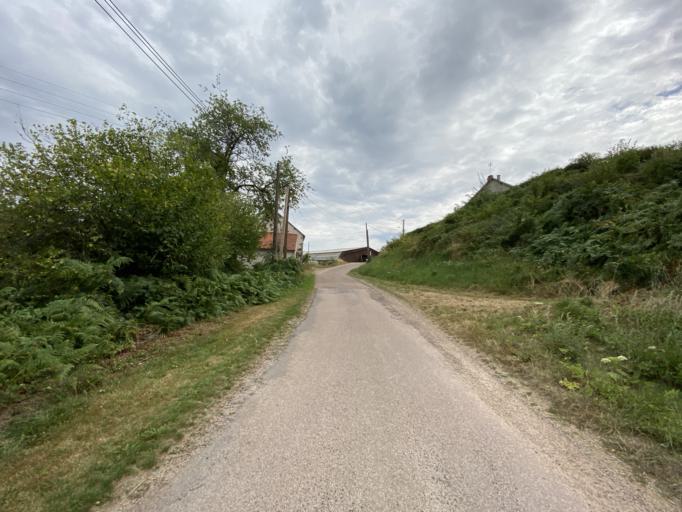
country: FR
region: Bourgogne
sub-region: Departement de la Cote-d'Or
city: Saulieu
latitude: 47.2588
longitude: 4.1353
